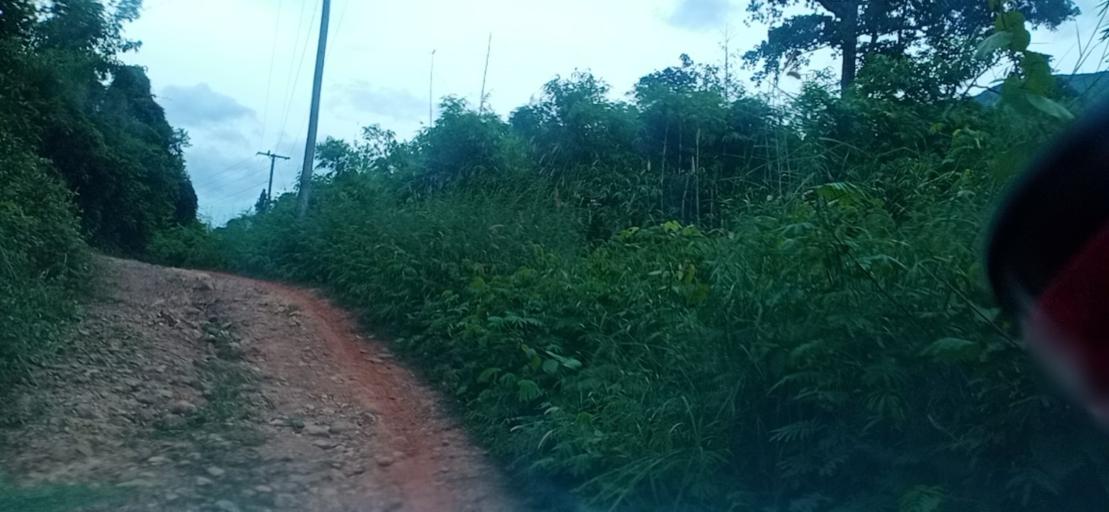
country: TH
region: Changwat Bueng Kan
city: Pak Khat
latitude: 18.5607
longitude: 103.2604
